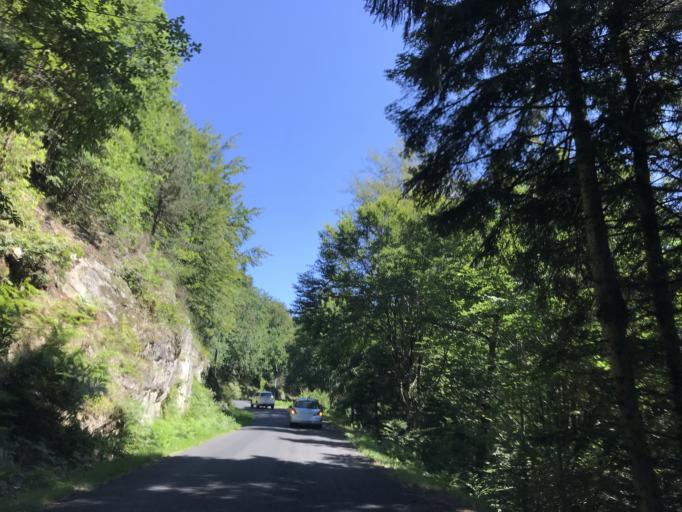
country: FR
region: Auvergne
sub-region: Departement du Puy-de-Dome
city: Job
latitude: 45.6647
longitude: 3.7213
